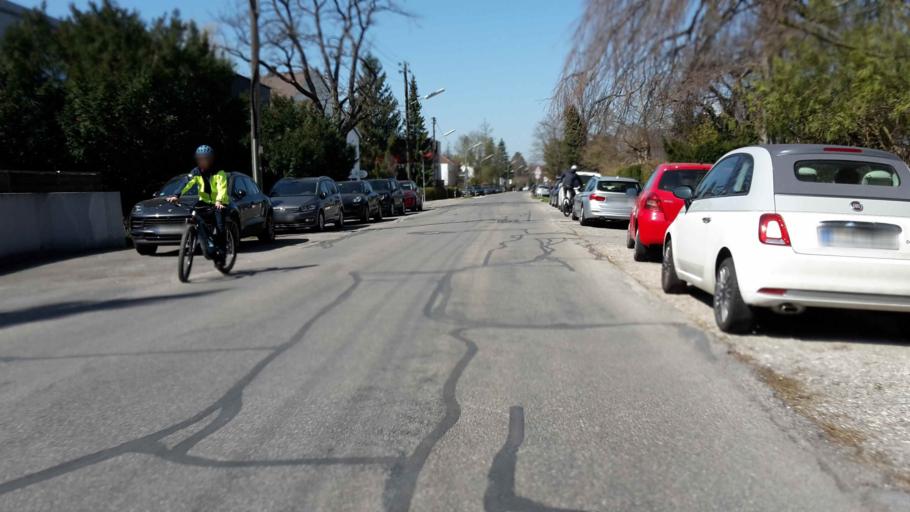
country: DE
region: Bavaria
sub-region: Upper Bavaria
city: Pasing
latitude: 48.1725
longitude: 11.4793
